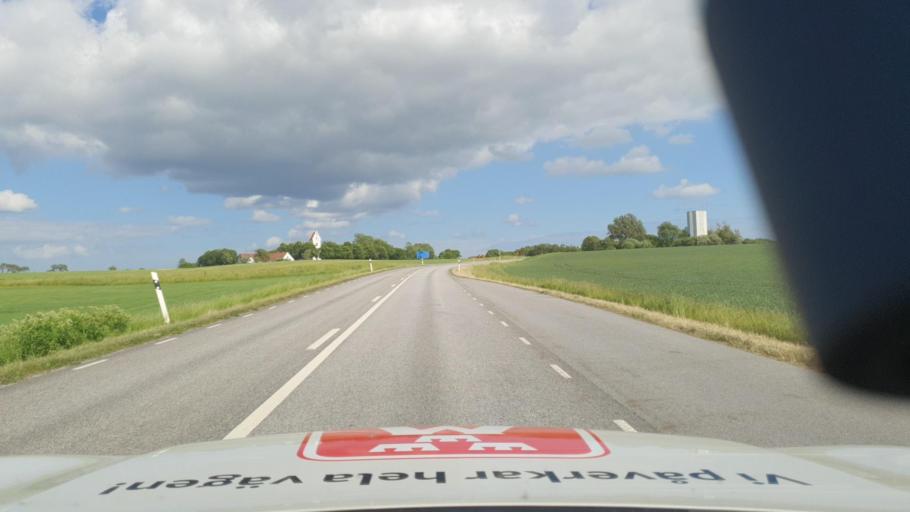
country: SE
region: Skane
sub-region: Simrishamns Kommun
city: Kivik
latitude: 55.5564
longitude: 14.1632
